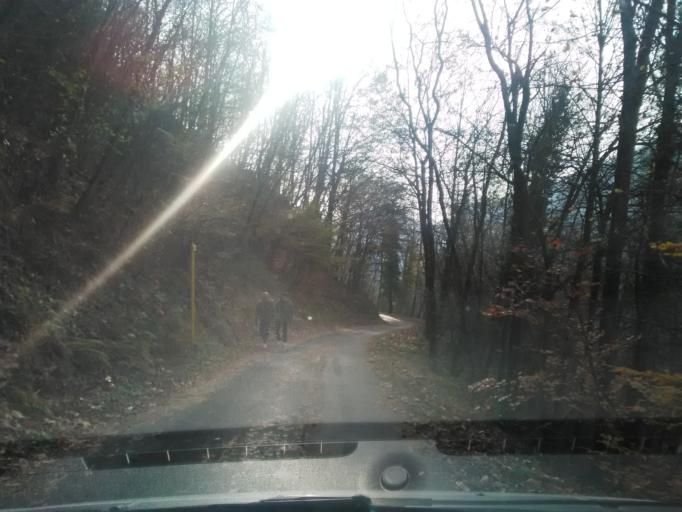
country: IT
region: Piedmont
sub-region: Provincia di Vercelli
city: Postua
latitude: 45.7079
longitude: 8.2335
